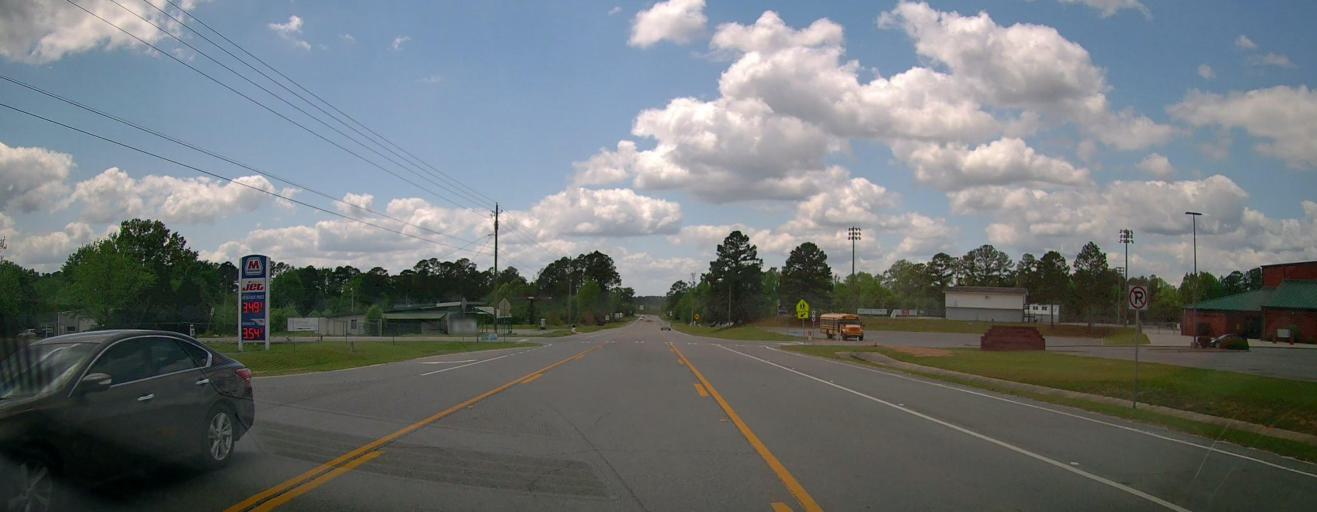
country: US
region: Georgia
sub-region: Laurens County
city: East Dublin
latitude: 32.5606
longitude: -82.8196
